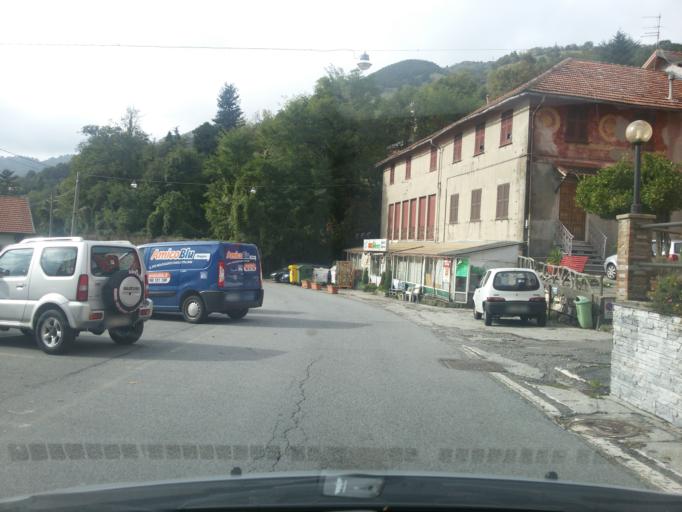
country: IT
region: Liguria
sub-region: Provincia di Genova
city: Davagna
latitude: 44.4809
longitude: 9.1195
